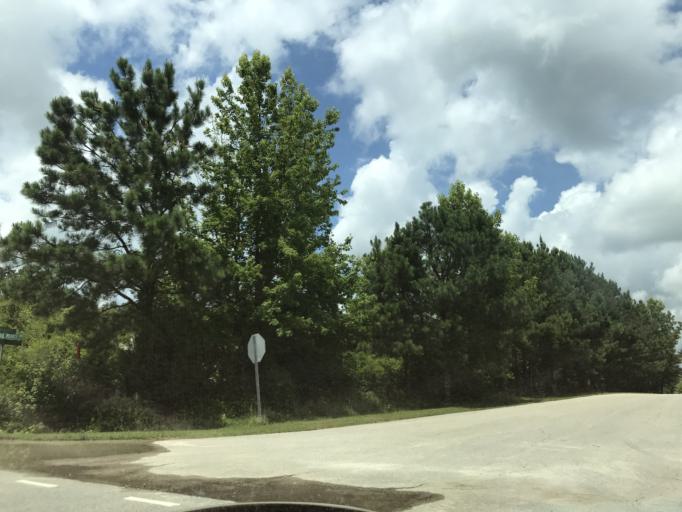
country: US
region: North Carolina
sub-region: Wake County
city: Rolesville
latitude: 35.9532
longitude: -78.3718
